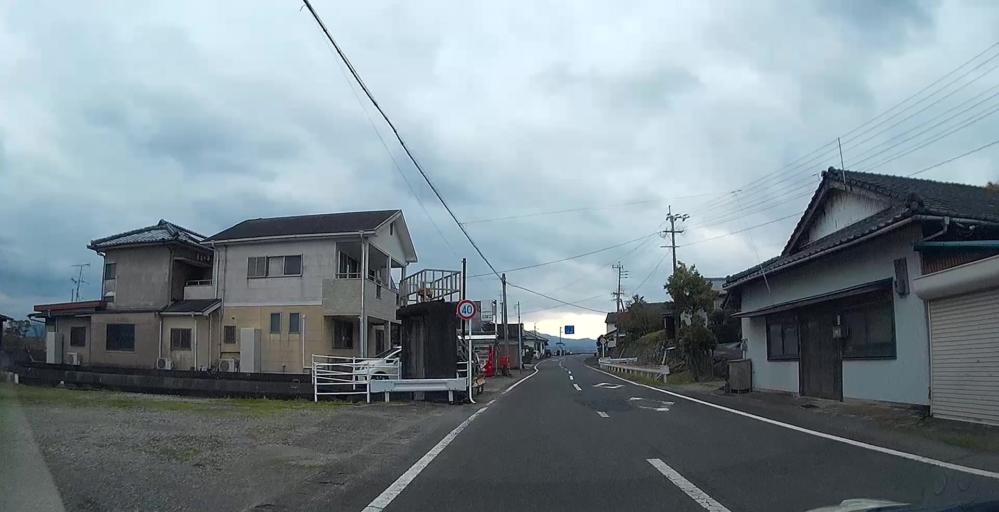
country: JP
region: Kagoshima
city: Izumi
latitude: 32.0937
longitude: 130.2740
